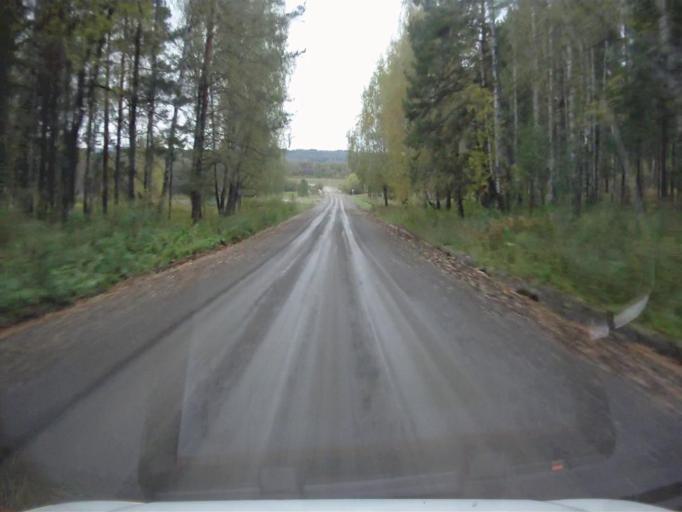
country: RU
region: Chelyabinsk
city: Nyazepetrovsk
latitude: 56.1225
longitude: 59.3600
